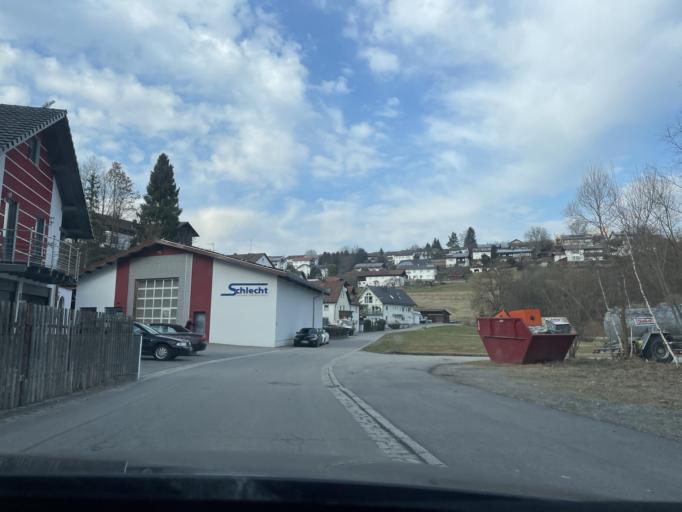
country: DE
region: Bavaria
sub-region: Lower Bavaria
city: Viechtach
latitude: 49.0835
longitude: 12.8867
